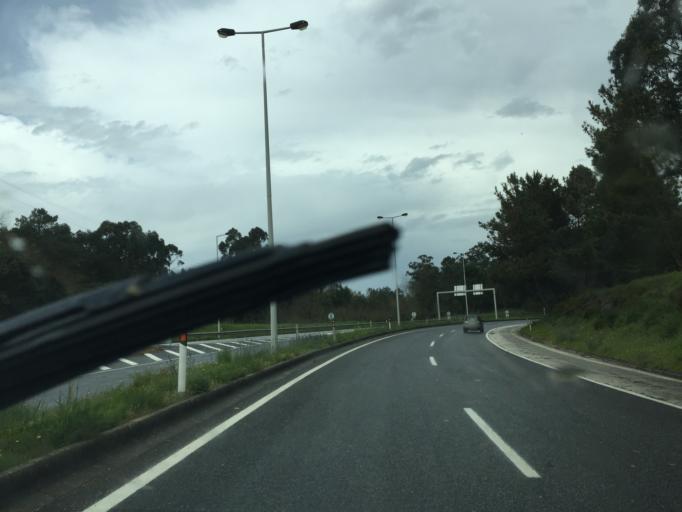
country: PT
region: Santarem
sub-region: Ourem
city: Fatima
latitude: 39.6308
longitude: -8.6837
